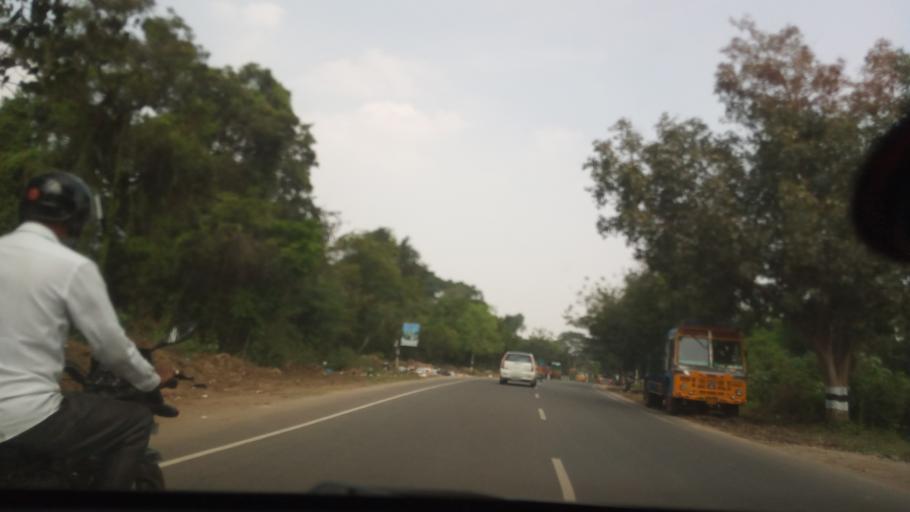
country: IN
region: Tamil Nadu
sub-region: Coimbatore
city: Perur
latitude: 11.0241
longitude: 76.8907
